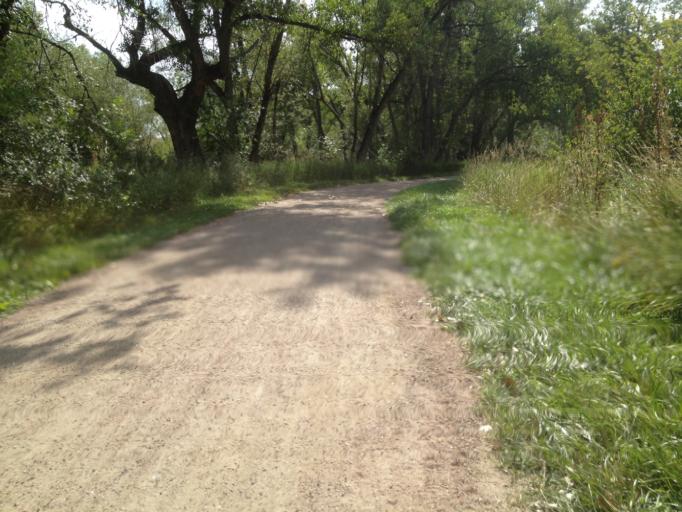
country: US
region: Colorado
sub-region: Boulder County
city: Lafayette
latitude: 39.9794
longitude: -105.1082
